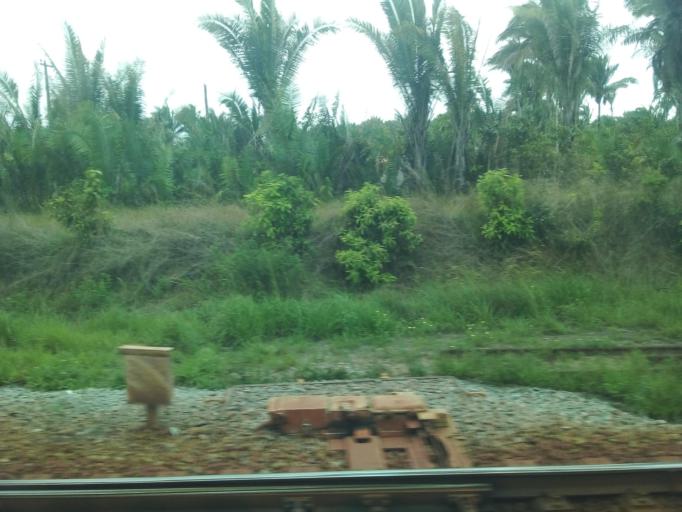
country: BR
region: Maranhao
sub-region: Santa Ines
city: Santa Ines
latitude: -3.6963
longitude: -45.3859
